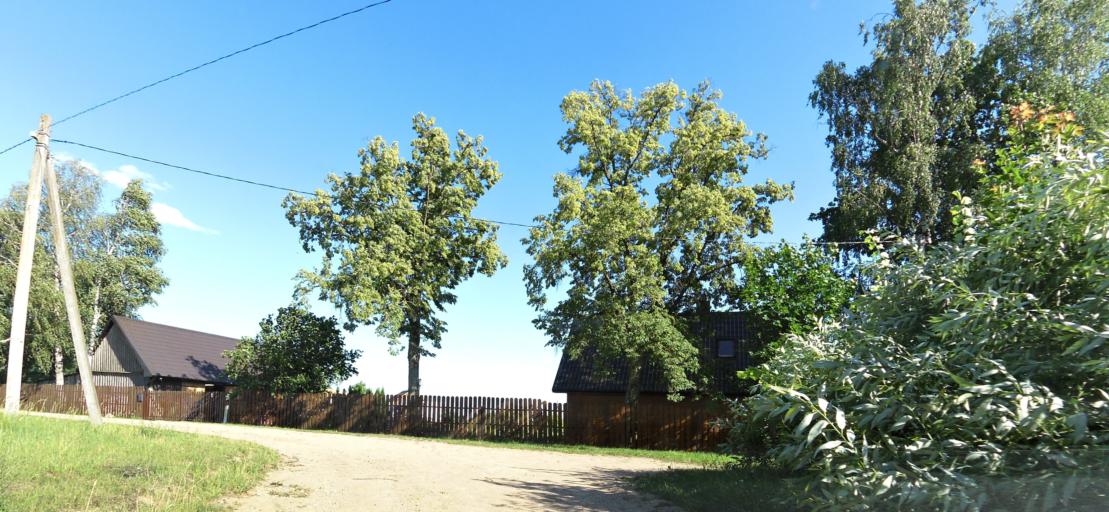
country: LT
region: Panevezys
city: Pasvalys
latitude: 56.1210
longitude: 24.4623
